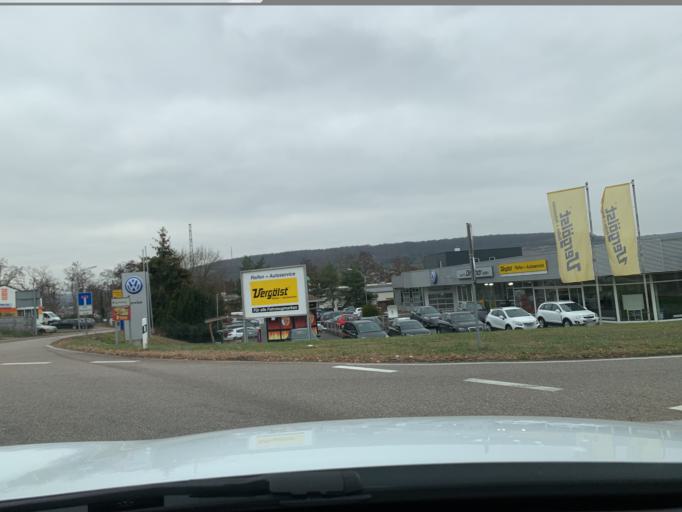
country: DE
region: Saarland
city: Kleinblittersdorf
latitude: 49.1679
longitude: 7.0338
